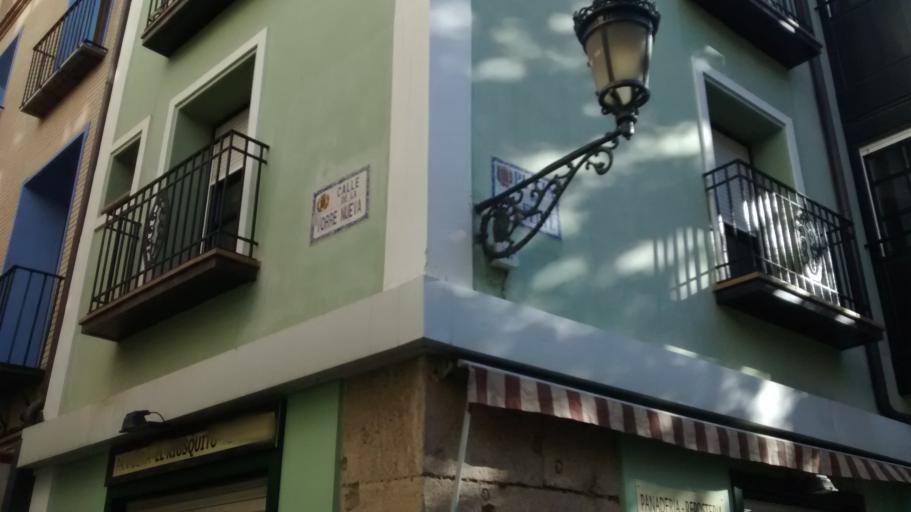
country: ES
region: Aragon
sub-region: Provincia de Zaragoza
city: Zaragoza
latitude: 41.6546
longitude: -0.8818
